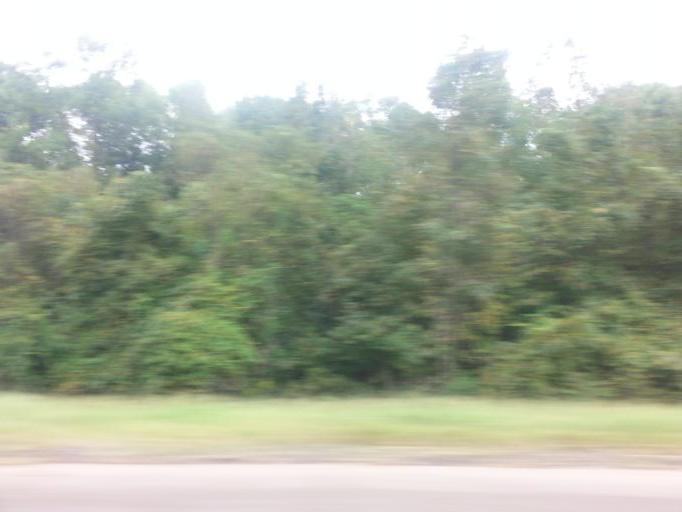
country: US
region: Alabama
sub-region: Butler County
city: Georgiana
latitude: 31.5591
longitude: -86.8663
